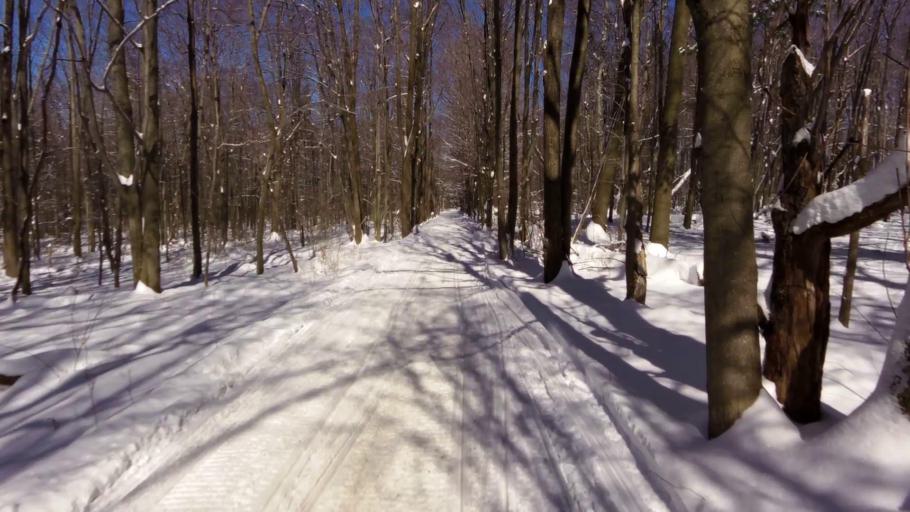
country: US
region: New York
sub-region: Chautauqua County
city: Mayville
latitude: 42.2345
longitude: -79.4204
